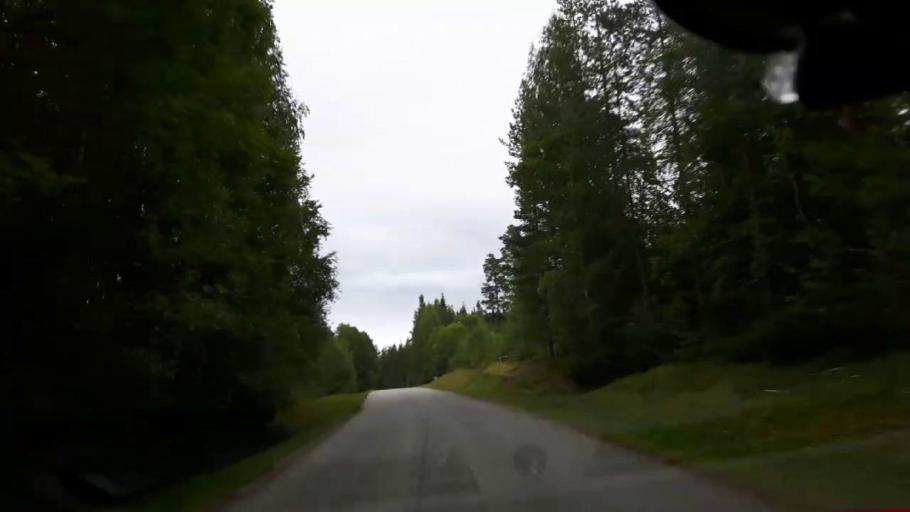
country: SE
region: Vaesternorrland
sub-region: Ange Kommun
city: Fransta
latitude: 62.7691
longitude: 16.0180
